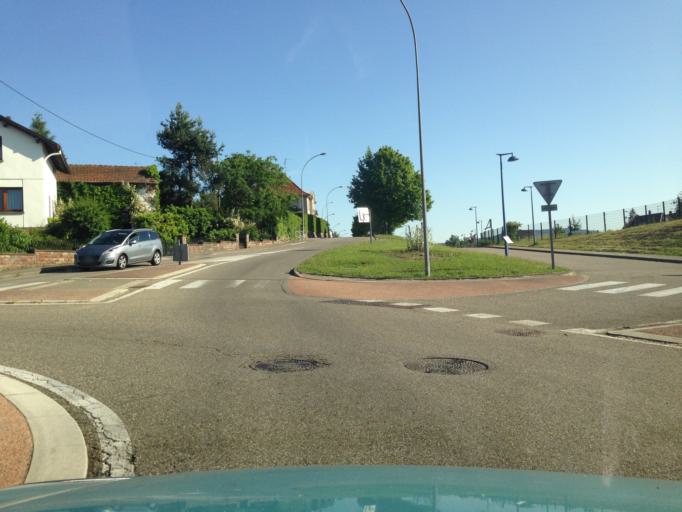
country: FR
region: Alsace
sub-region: Departement du Bas-Rhin
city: Ingwiller
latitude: 48.8697
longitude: 7.4760
